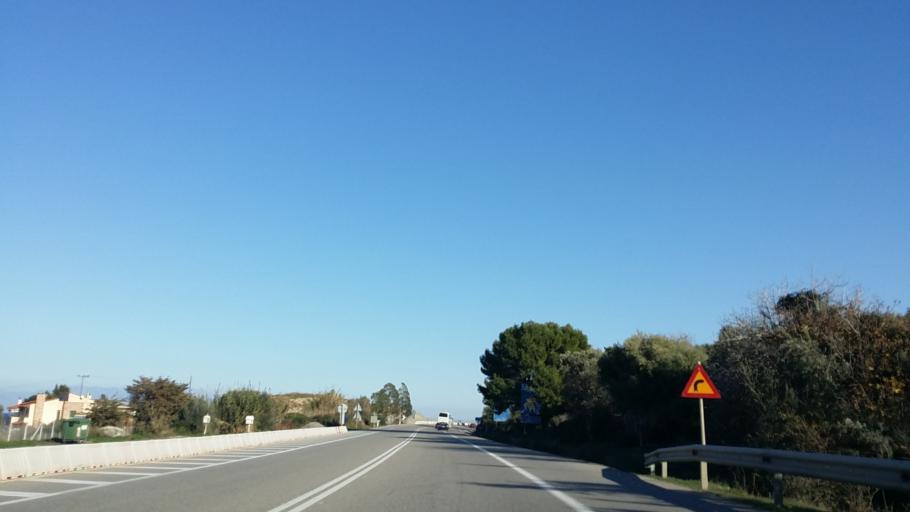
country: GR
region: West Greece
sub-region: Nomos Achaias
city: Aiyira
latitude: 38.1409
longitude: 22.3755
